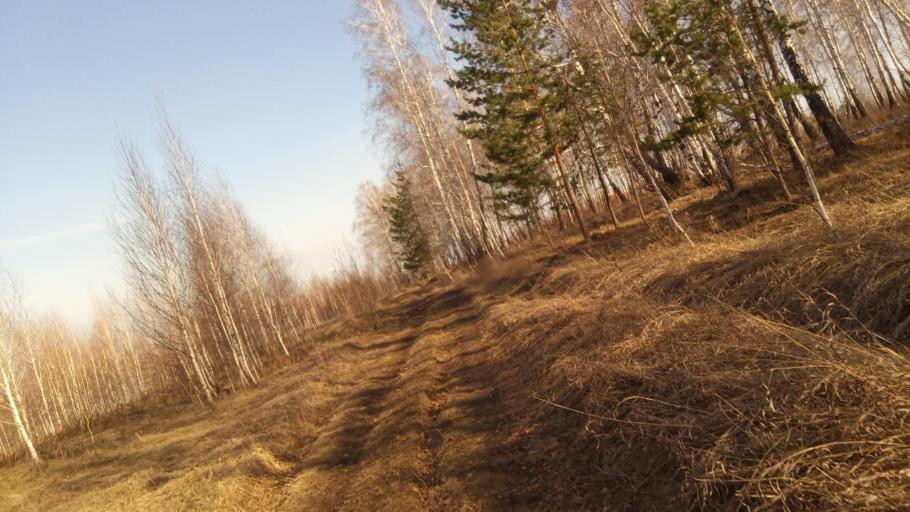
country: RU
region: Chelyabinsk
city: Sargazy
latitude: 55.1145
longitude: 61.2430
